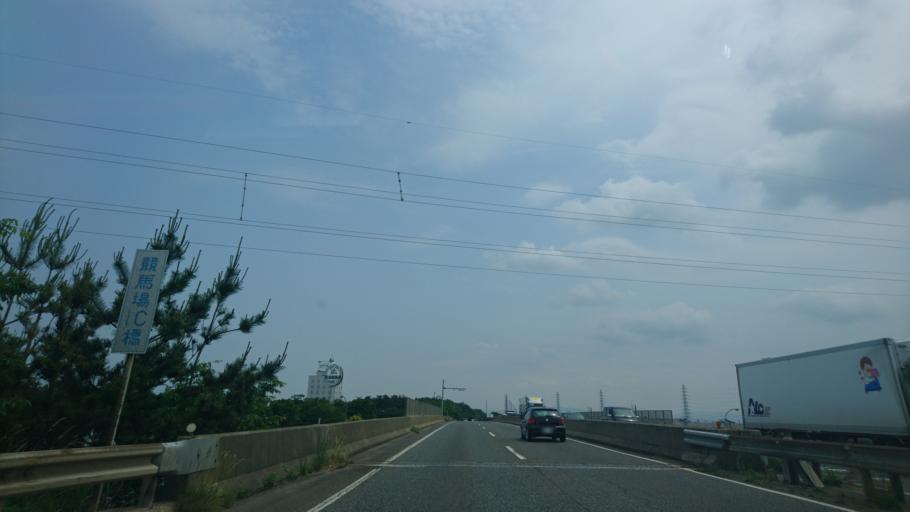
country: JP
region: Niigata
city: Kameda-honcho
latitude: 37.9421
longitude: 139.1831
